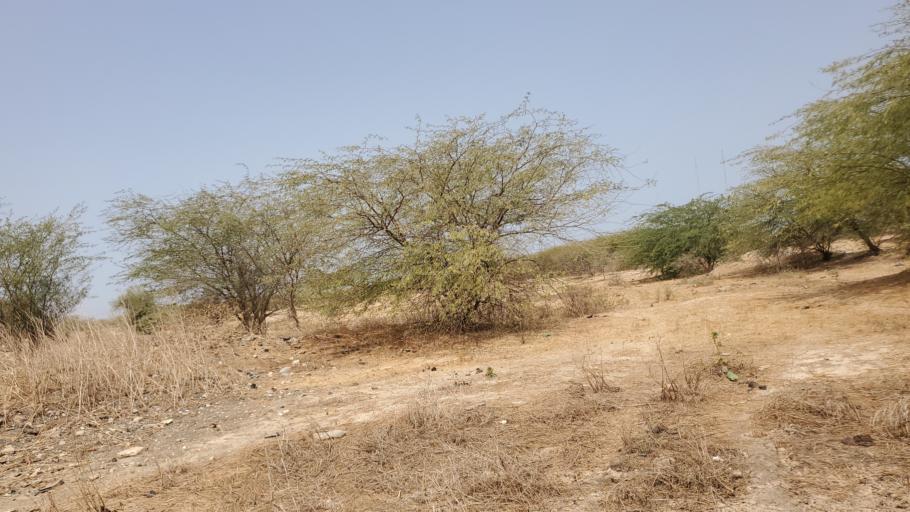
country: SN
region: Saint-Louis
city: Saint-Louis
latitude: 15.9526
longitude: -16.4320
